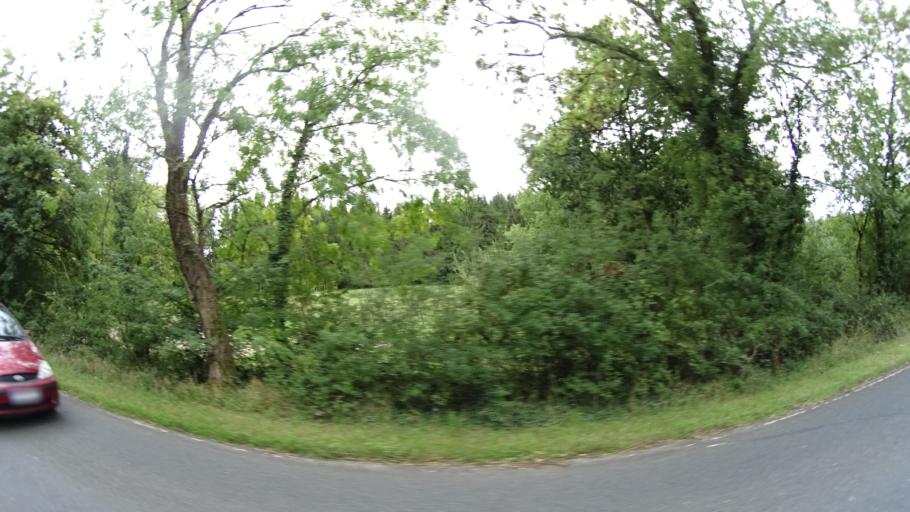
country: GB
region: England
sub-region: Dorset
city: Shaftesbury
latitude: 51.0152
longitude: -2.2152
